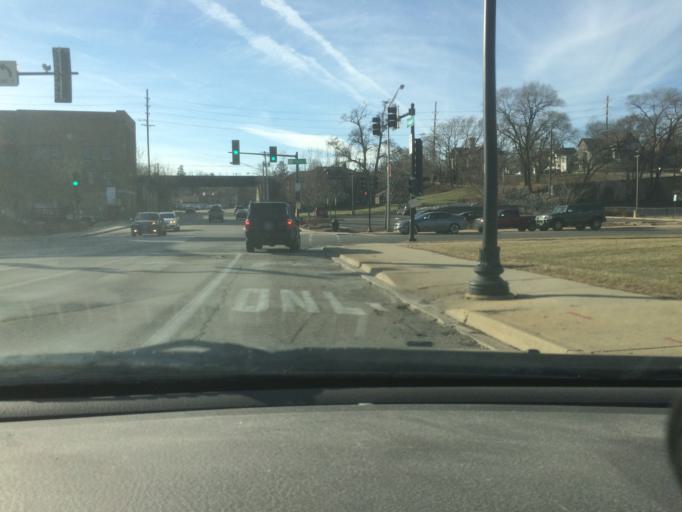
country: US
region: Illinois
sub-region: Kane County
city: Elgin
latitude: 42.0374
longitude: -88.2874
